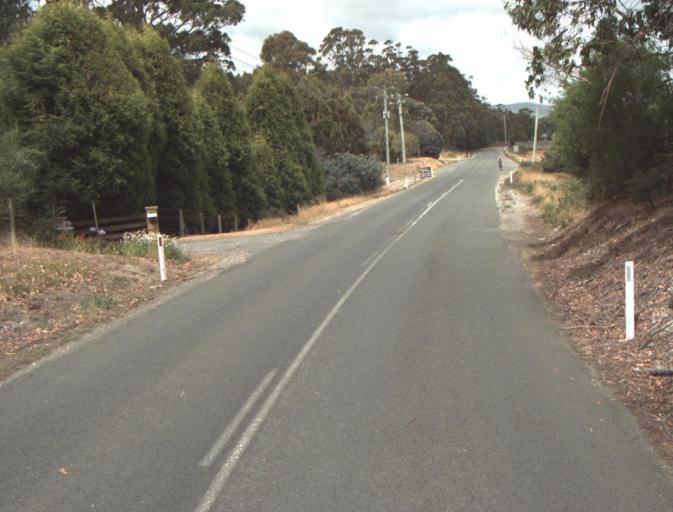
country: AU
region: Tasmania
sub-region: Launceston
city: Mayfield
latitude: -41.2086
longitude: 147.2148
